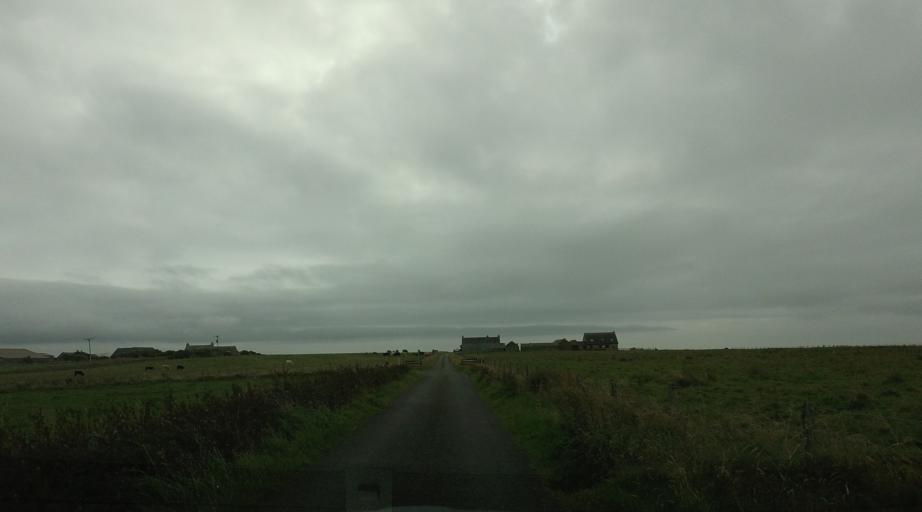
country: GB
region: Scotland
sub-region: Orkney Islands
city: Orkney
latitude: 58.7645
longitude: -2.9616
